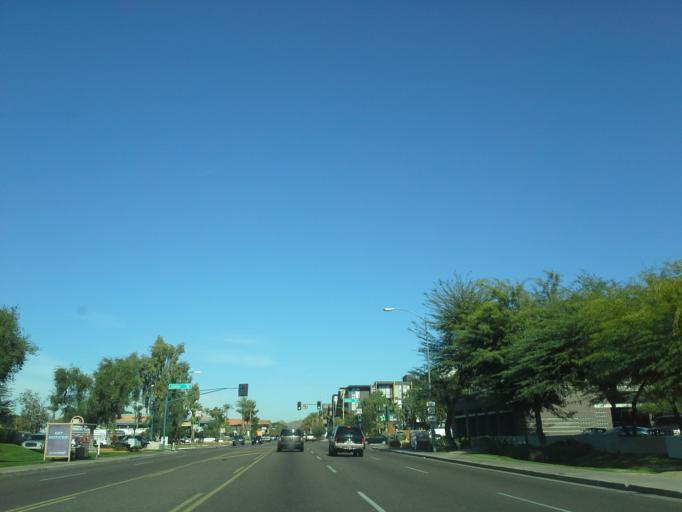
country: US
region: Arizona
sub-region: Maricopa County
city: Phoenix
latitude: 33.5120
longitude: -112.0475
